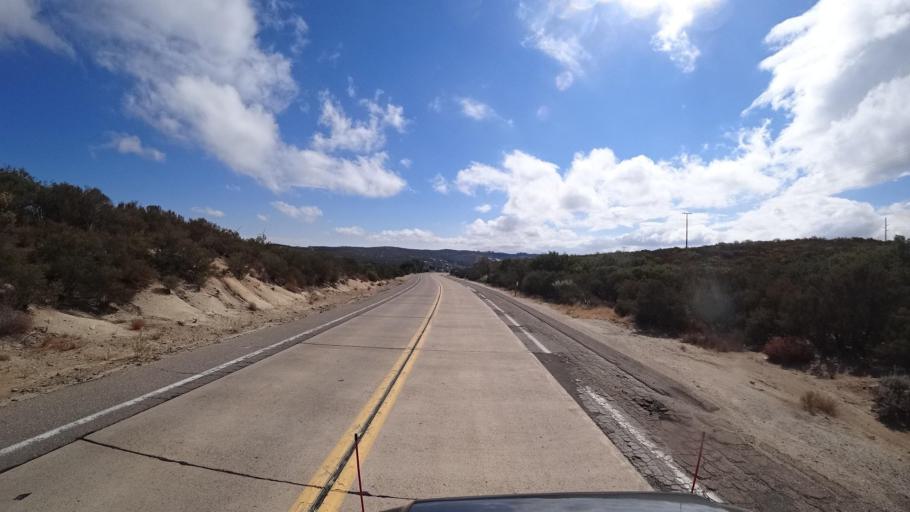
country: US
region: California
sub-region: San Diego County
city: Campo
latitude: 32.6969
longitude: -116.3507
